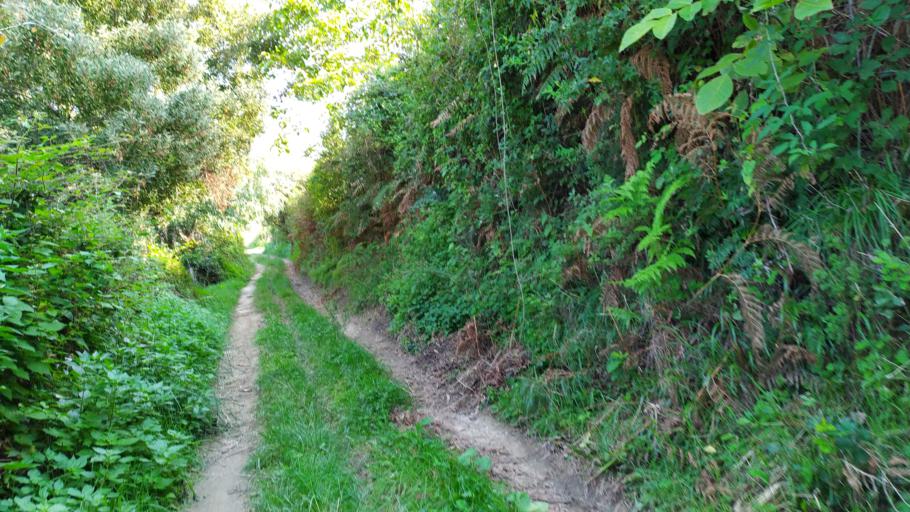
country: IT
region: Sicily
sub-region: Messina
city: Condro
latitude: 38.1617
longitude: 15.3335
